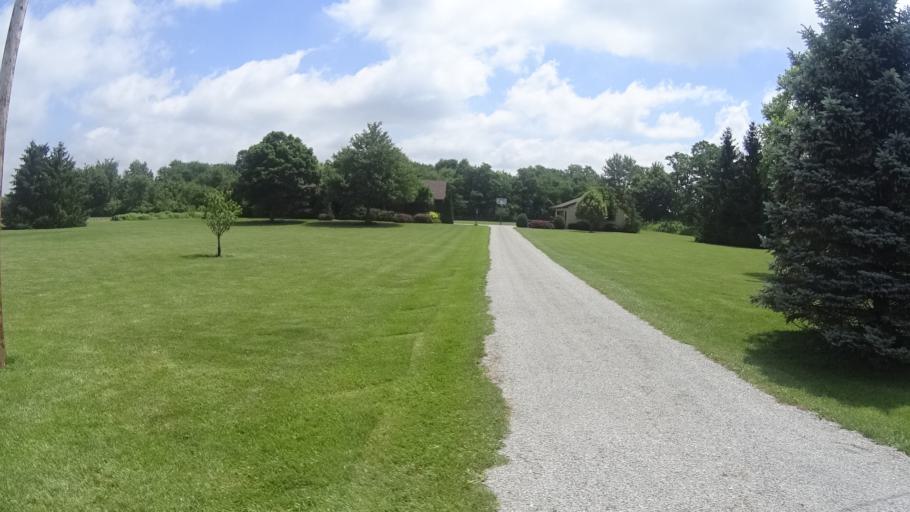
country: US
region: Ohio
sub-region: Huron County
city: Wakeman
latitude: 41.2880
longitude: -82.3626
